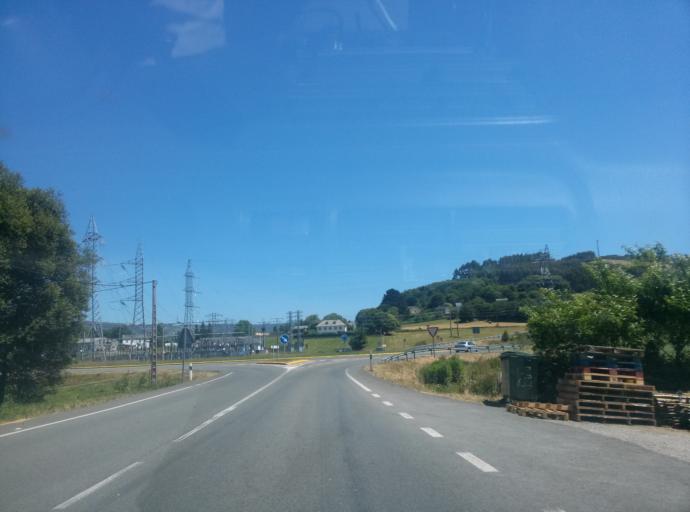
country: ES
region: Galicia
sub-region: Provincia de Lugo
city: Meira
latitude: 43.2218
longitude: -7.3208
